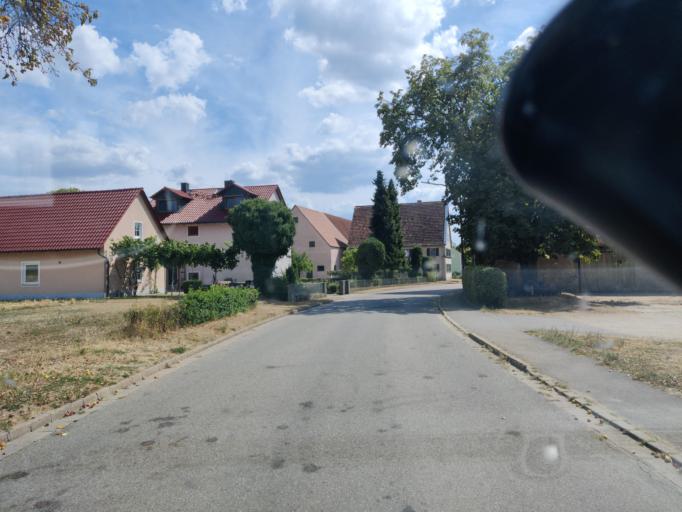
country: DE
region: Bavaria
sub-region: Regierungsbezirk Mittelfranken
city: Heideck
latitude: 49.1209
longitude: 11.1319
